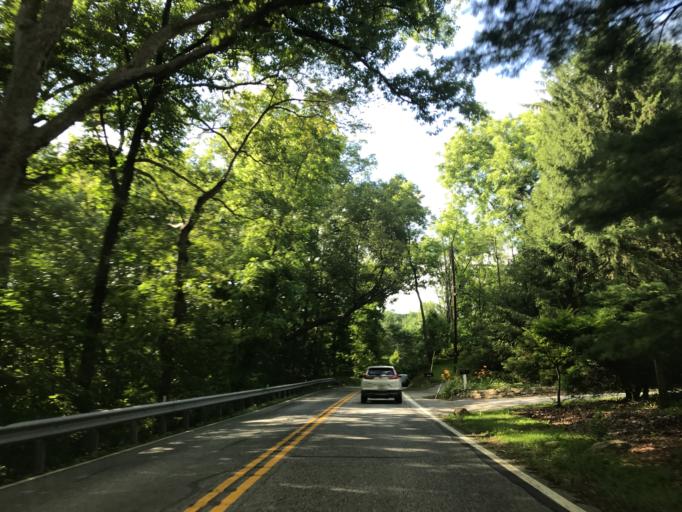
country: US
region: Maryland
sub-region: Carroll County
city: Hampstead
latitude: 39.5848
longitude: -76.7647
